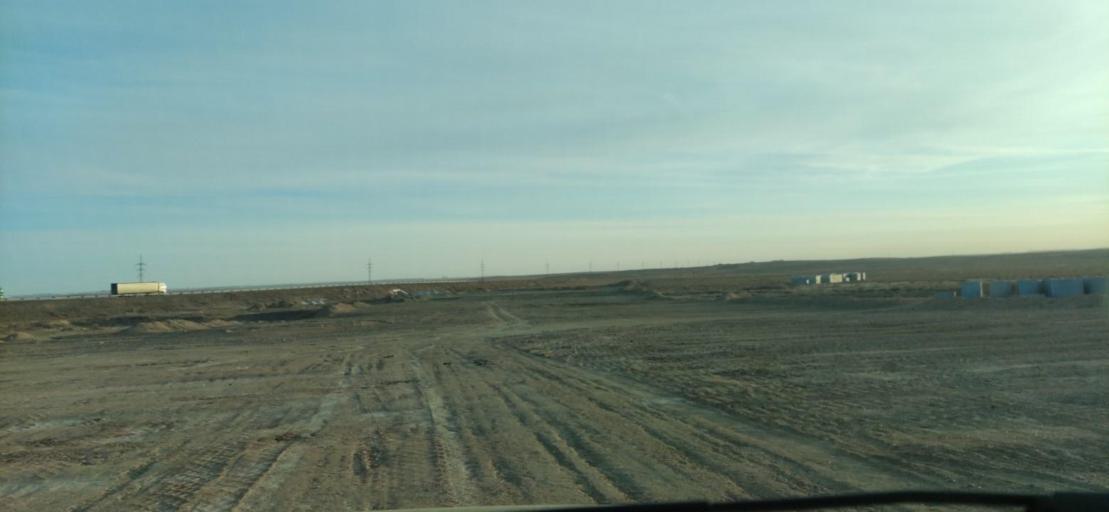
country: KZ
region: Qaraghandy
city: Saryshaghan
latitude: 46.0932
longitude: 73.6054
